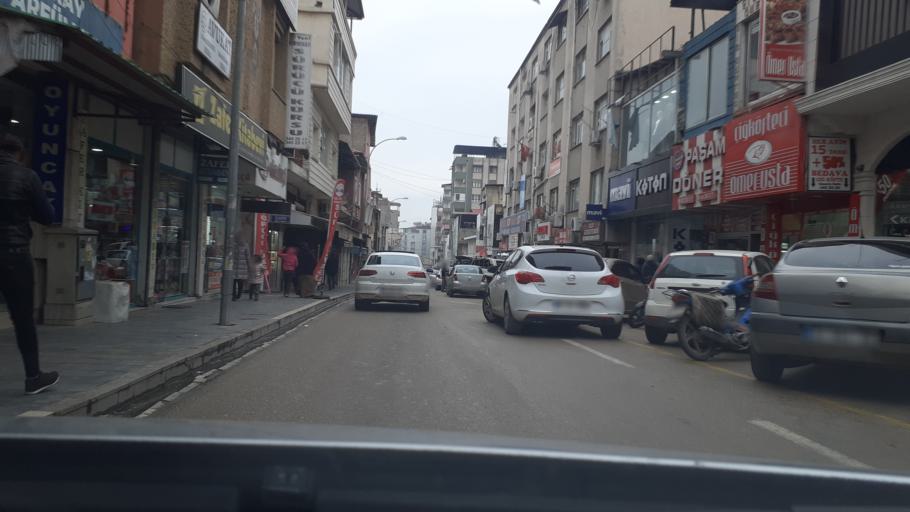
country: TR
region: Hatay
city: Kirikhan
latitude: 36.4990
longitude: 36.3546
